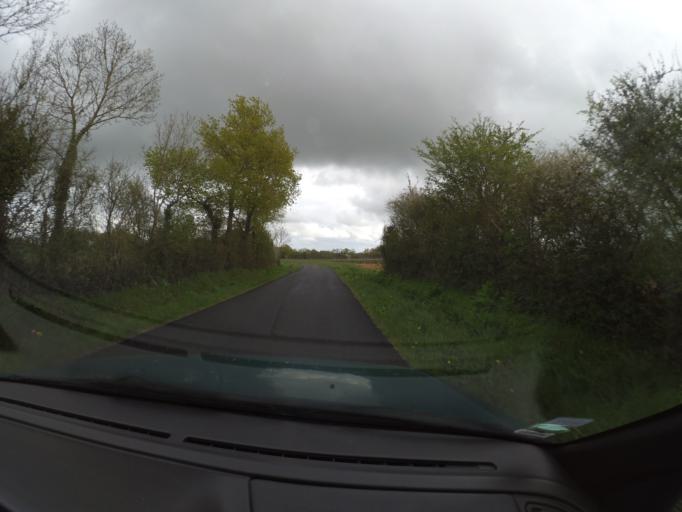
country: FR
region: Pays de la Loire
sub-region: Departement de la Loire-Atlantique
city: Maisdon-sur-Sevre
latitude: 47.0816
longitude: -1.3705
